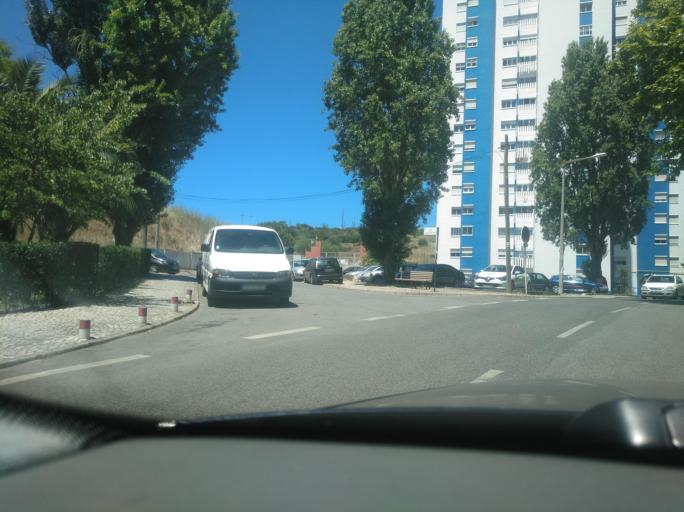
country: PT
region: Lisbon
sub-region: Odivelas
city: Ramada
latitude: 38.8118
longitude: -9.1794
